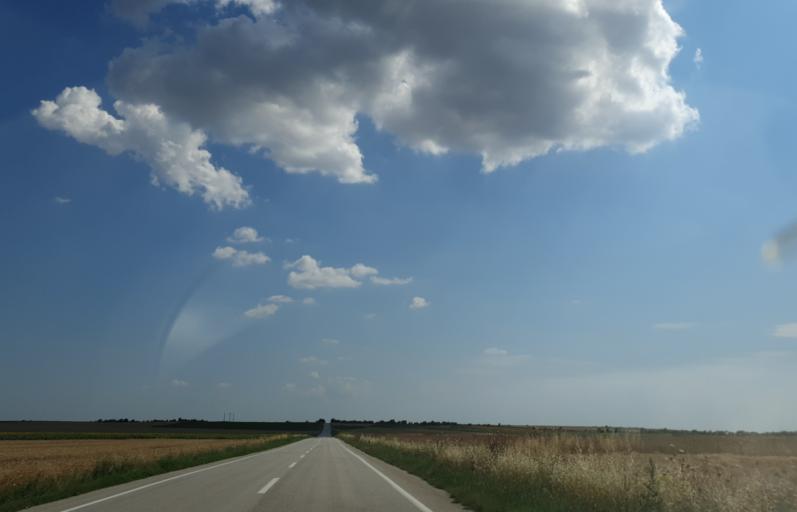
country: TR
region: Kirklareli
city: Buyukkaristiran
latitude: 41.3924
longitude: 27.5722
